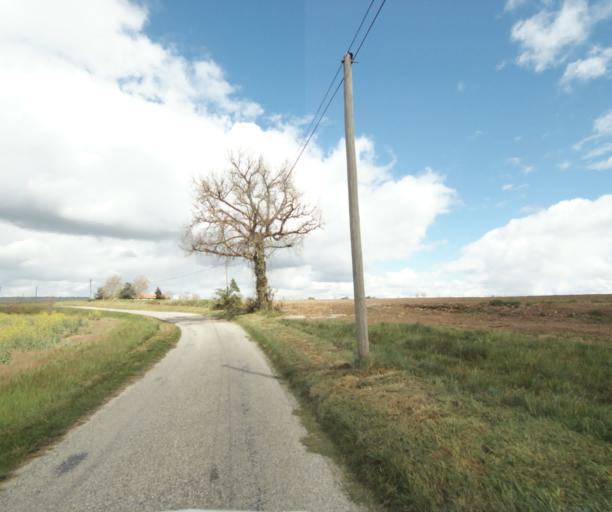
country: FR
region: Midi-Pyrenees
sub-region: Departement de l'Ariege
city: Saverdun
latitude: 43.2628
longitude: 1.5842
